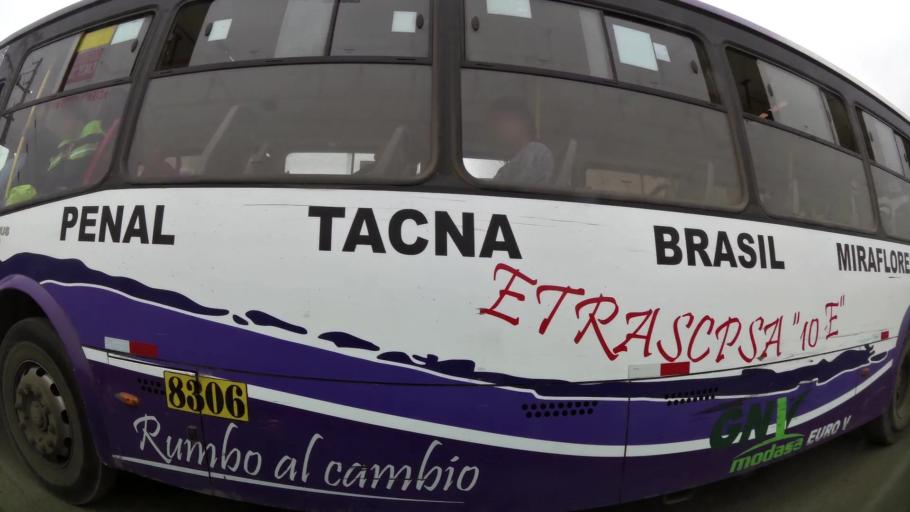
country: PE
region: Lima
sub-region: Lima
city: Surco
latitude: -12.2224
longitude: -76.9241
